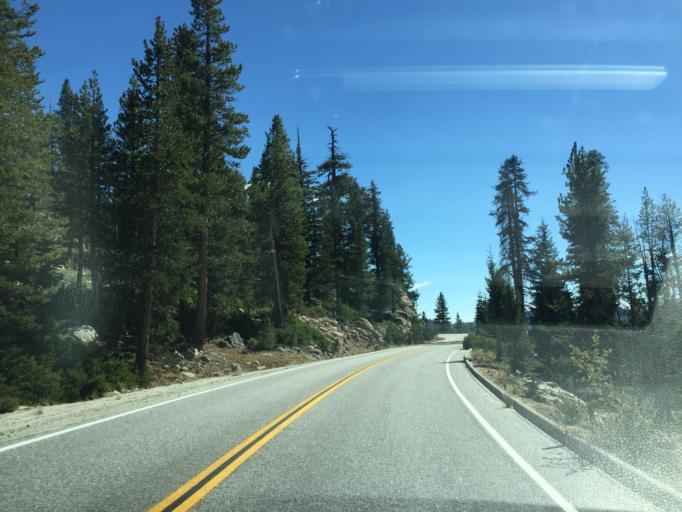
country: US
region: California
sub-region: Mariposa County
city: Yosemite Valley
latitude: 37.8459
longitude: -119.5949
